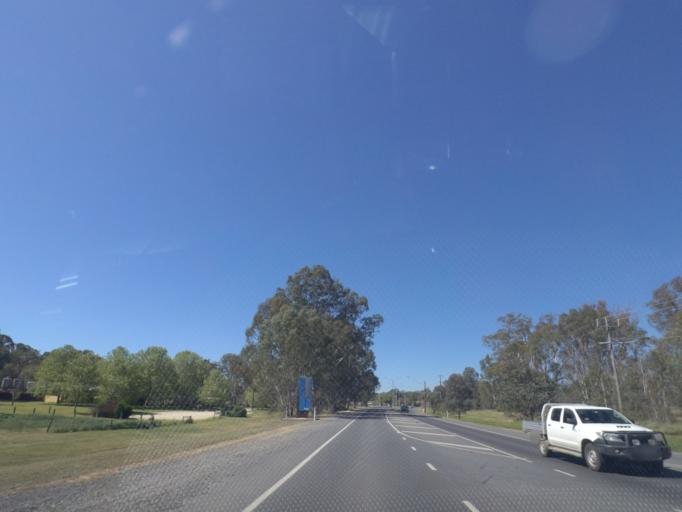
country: AU
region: Victoria
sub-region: Murrindindi
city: Kinglake West
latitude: -37.0235
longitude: 145.1140
